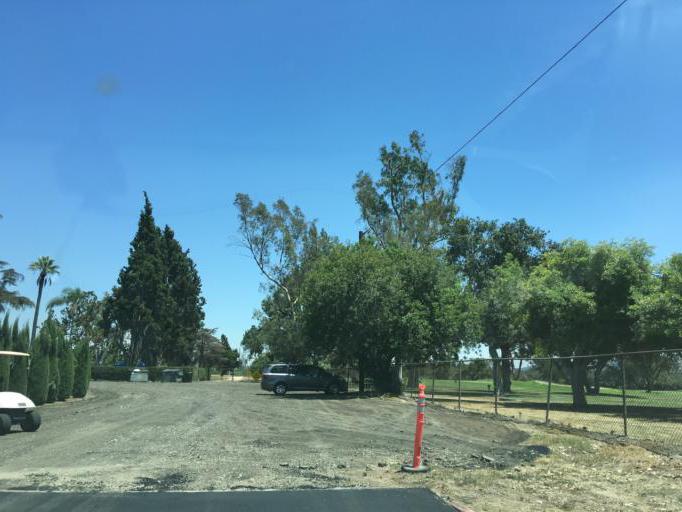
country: US
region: California
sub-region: Los Angeles County
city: South San Gabriel
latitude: 34.0518
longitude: -118.0768
